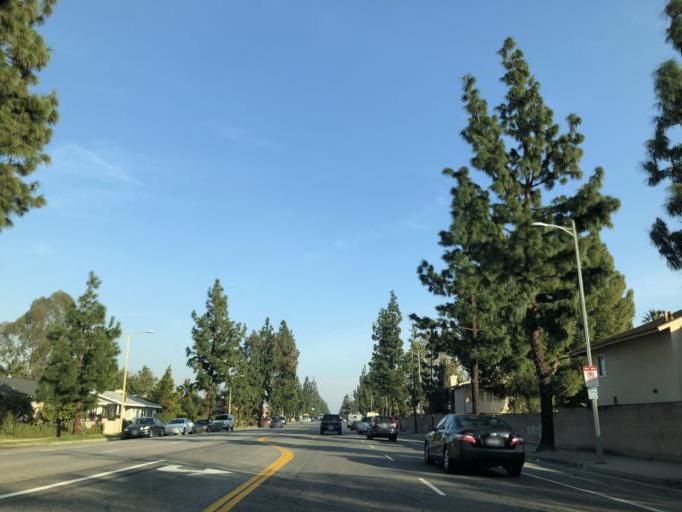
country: US
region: California
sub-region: Los Angeles County
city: Chatsworth
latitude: 34.2572
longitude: -118.5837
